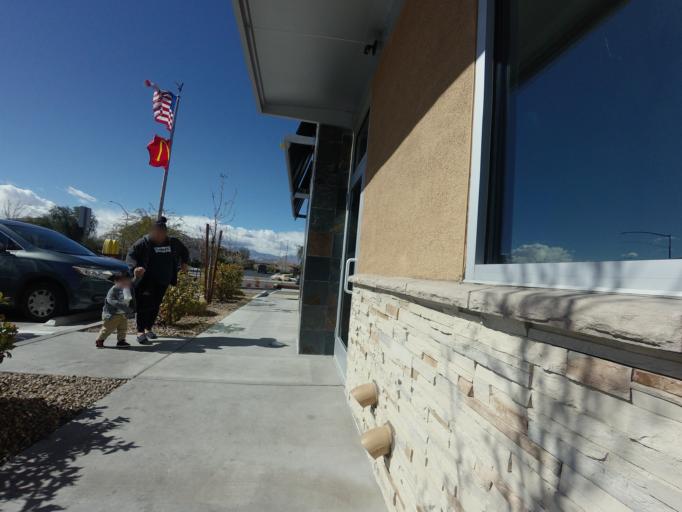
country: US
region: Nevada
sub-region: Clark County
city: Nellis Air Force Base
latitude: 36.2647
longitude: -115.1166
